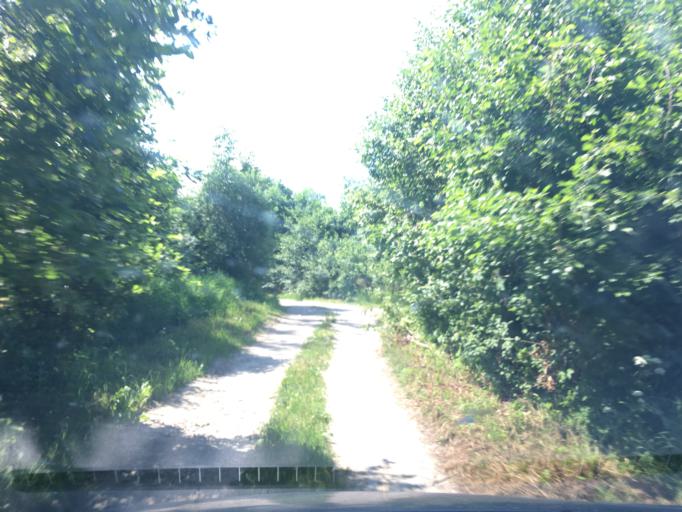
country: EE
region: Laeaene
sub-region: Lihula vald
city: Lihula
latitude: 58.7344
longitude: 24.1580
